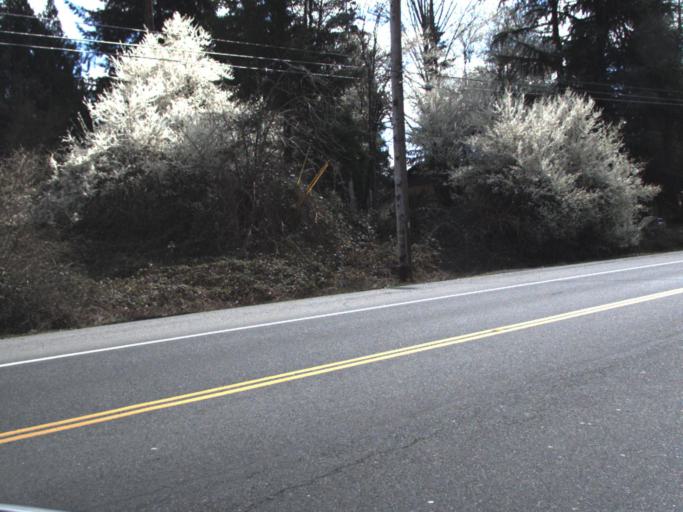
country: US
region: Washington
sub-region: King County
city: Maple Valley
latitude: 47.4071
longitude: -122.0382
